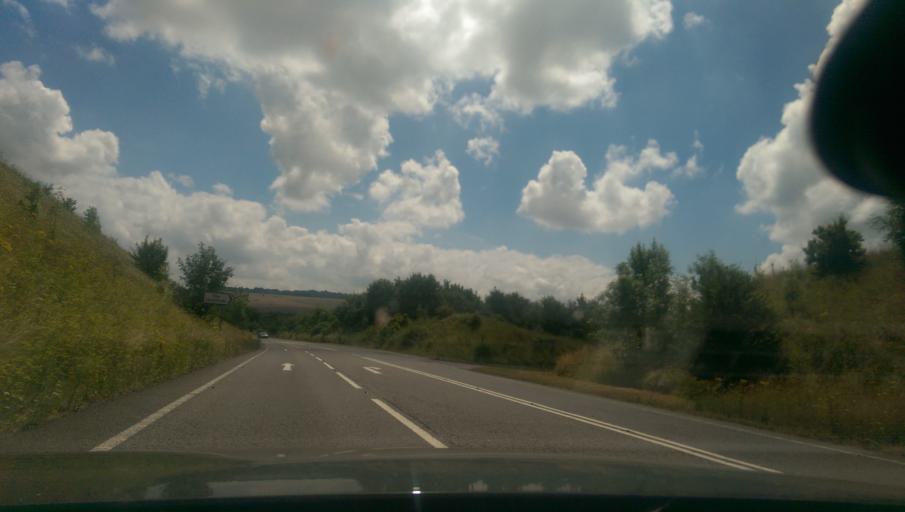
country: GB
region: England
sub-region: Wiltshire
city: Stapleford
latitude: 51.1368
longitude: -1.9428
